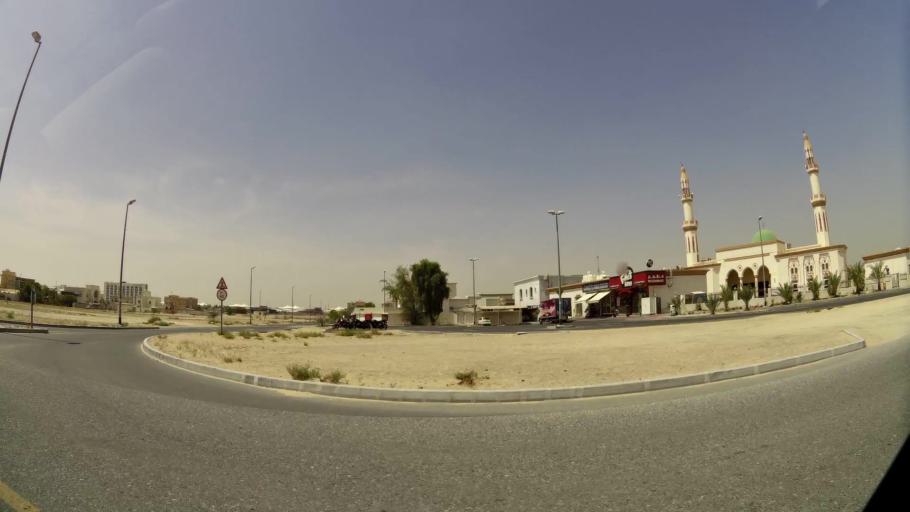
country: AE
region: Ash Shariqah
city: Sharjah
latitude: 25.1807
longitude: 55.4176
